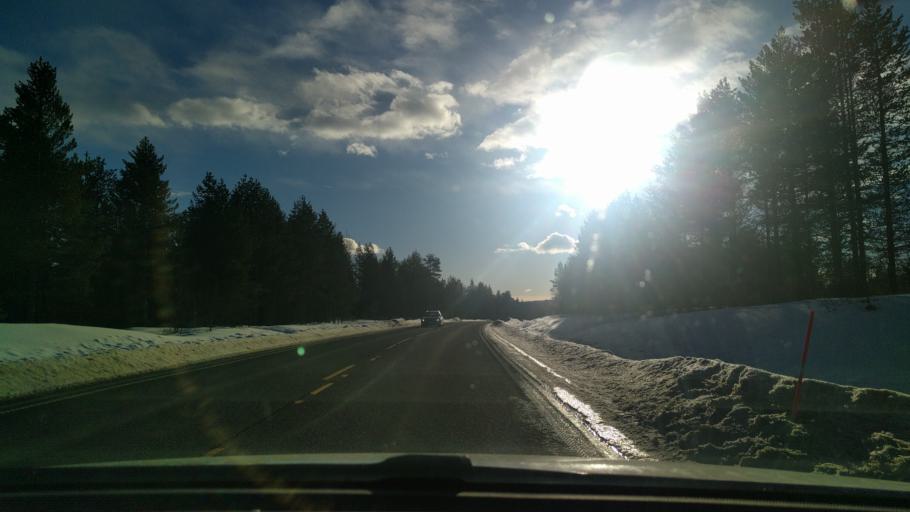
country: NO
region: Hedmark
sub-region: Trysil
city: Innbygda
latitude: 61.1093
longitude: 12.0376
